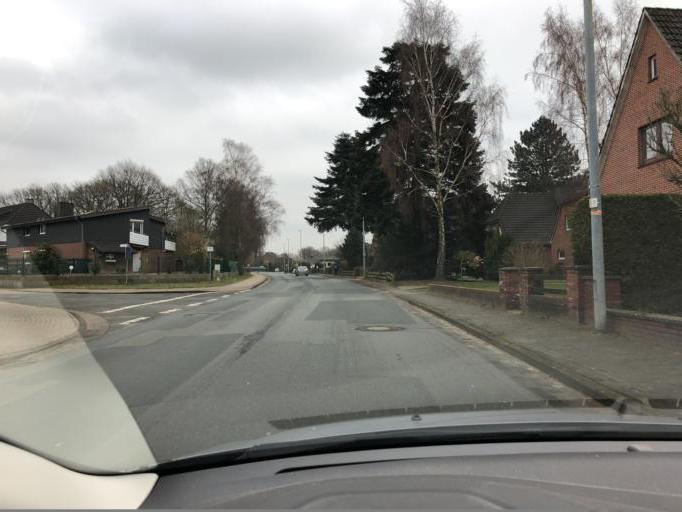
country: DE
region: Lower Saxony
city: Ganderkesee
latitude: 53.0888
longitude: 8.5335
